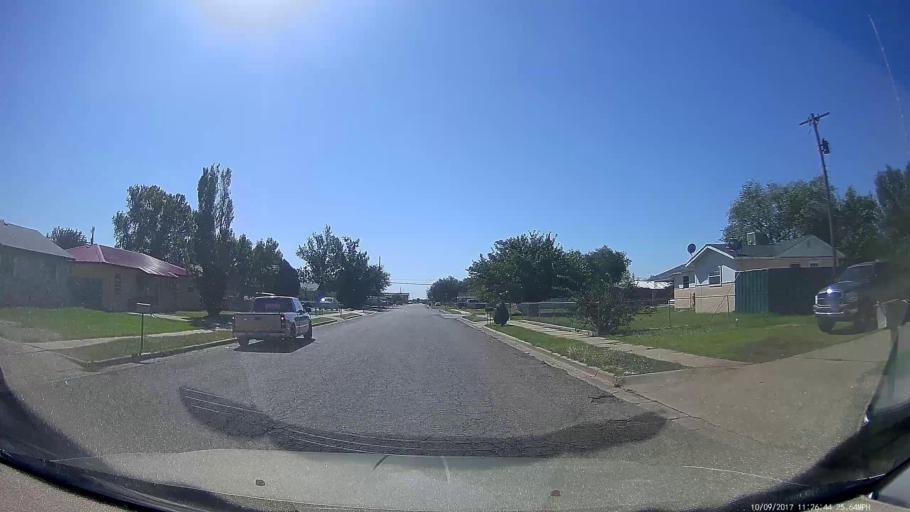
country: US
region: New Mexico
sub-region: Curry County
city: Clovis
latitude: 34.4088
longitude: -103.2272
